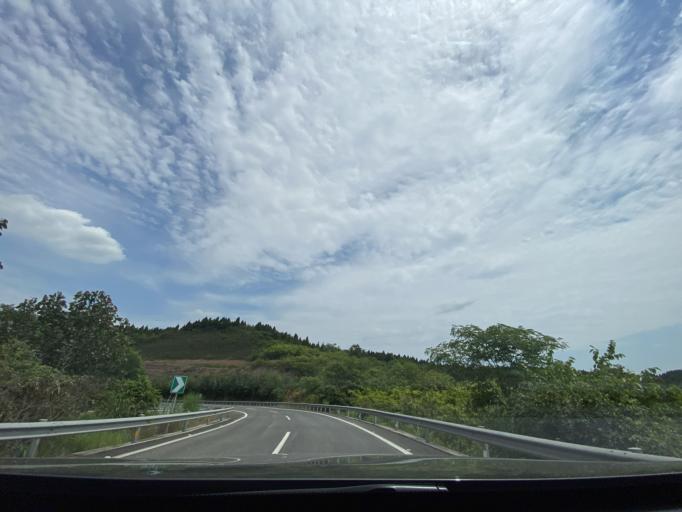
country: CN
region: Sichuan
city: Mianyang
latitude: 31.3500
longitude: 104.7062
